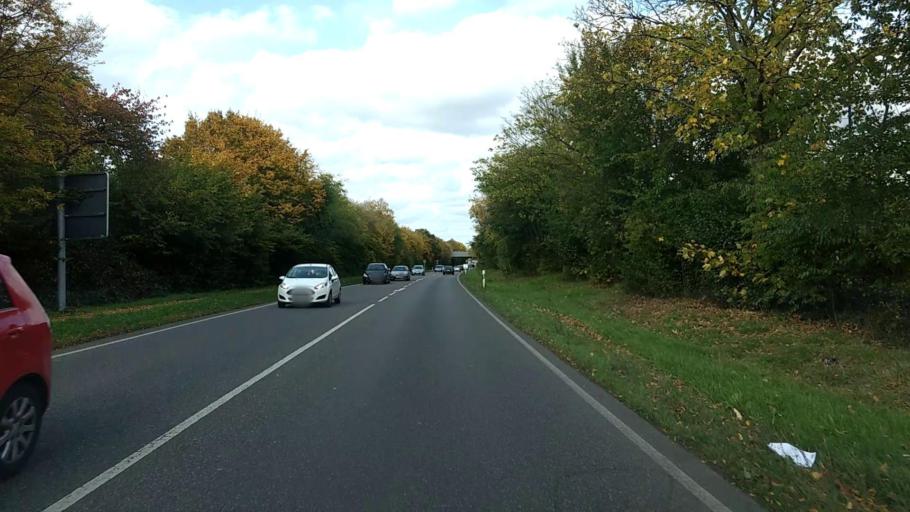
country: DE
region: North Rhine-Westphalia
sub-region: Regierungsbezirk Koln
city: Kerpen
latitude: 50.9013
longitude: 6.6836
